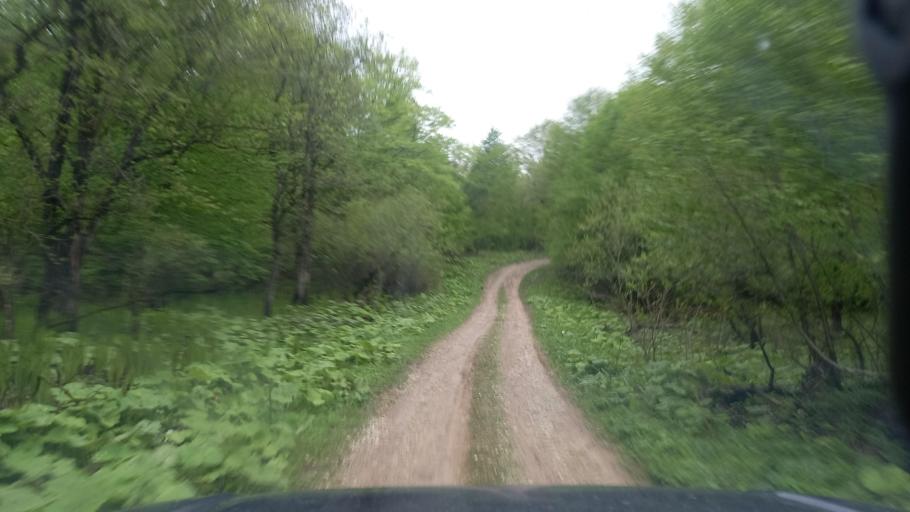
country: RU
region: Kabardino-Balkariya
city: Babugent
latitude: 43.2176
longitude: 43.5524
